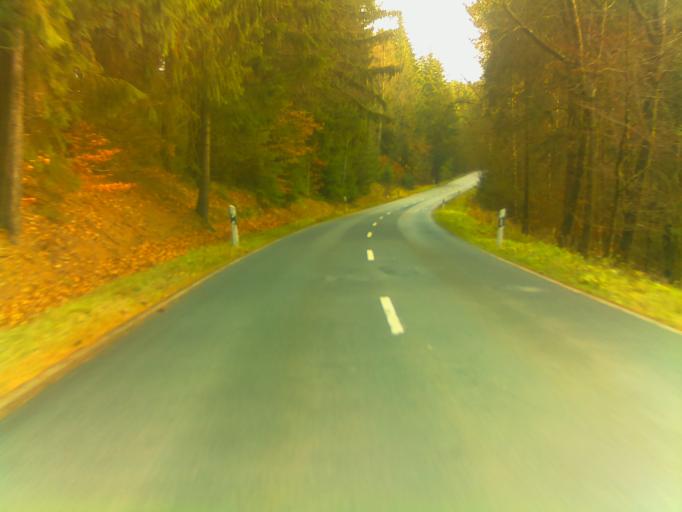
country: DE
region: Thuringia
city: Schleusingen
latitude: 50.4720
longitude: 10.7664
